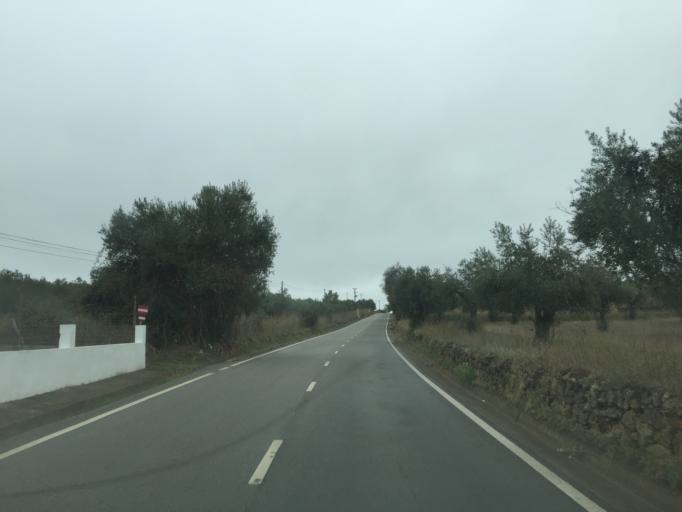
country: PT
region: Portalegre
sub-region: Alter do Chao
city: Alter do Chao
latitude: 39.2082
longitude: -7.6565
